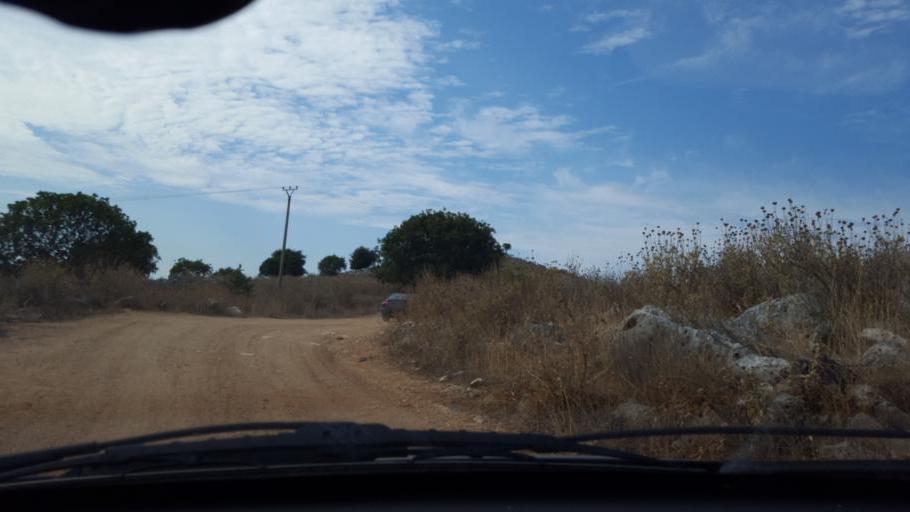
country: AL
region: Vlore
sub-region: Rrethi i Sarandes
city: Xarre
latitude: 39.7550
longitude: 19.9808
